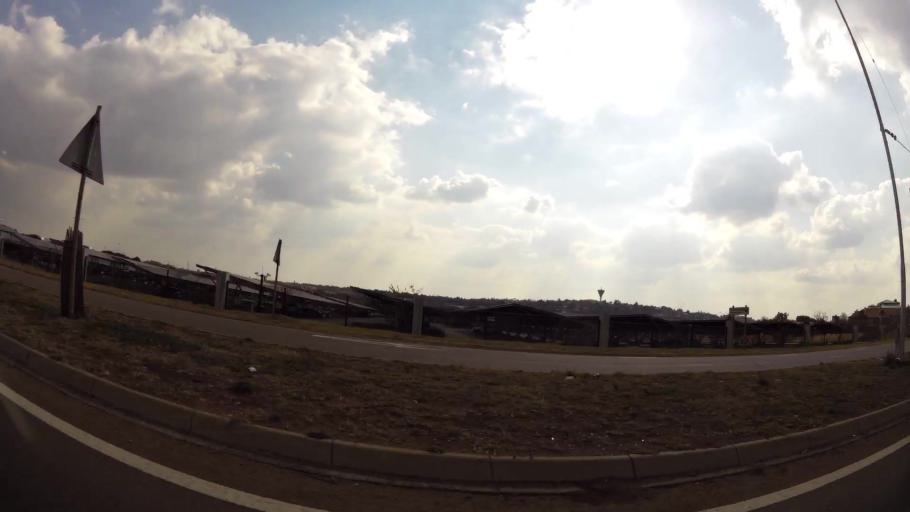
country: ZA
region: Gauteng
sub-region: City of Tshwane Metropolitan Municipality
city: Centurion
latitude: -25.8763
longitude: 28.1915
